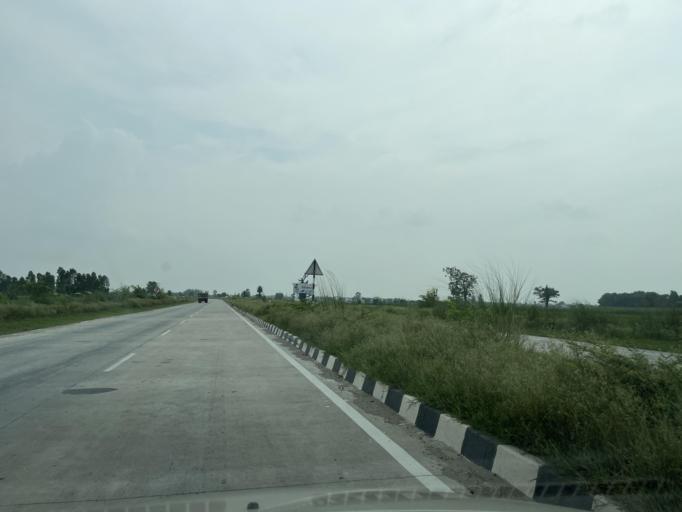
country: IN
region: Uttarakhand
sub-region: Udham Singh Nagar
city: Kashipur
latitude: 29.1828
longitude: 78.9395
